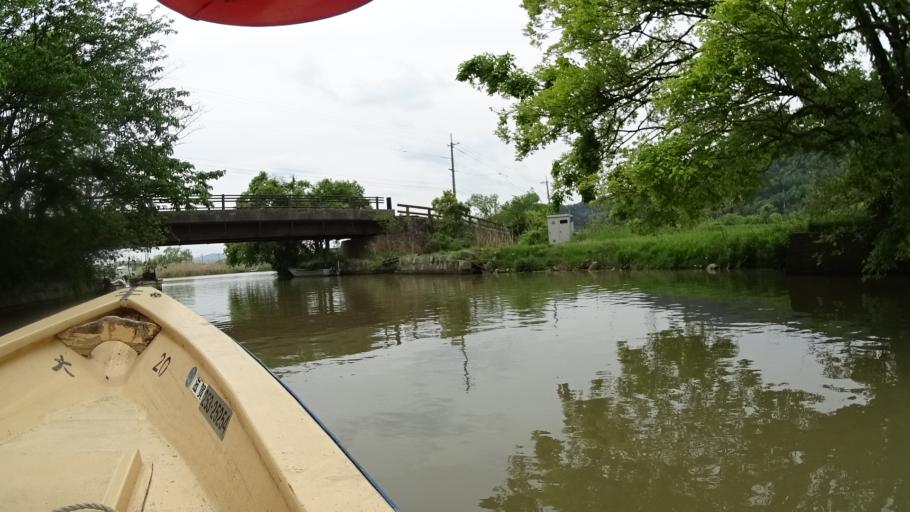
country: JP
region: Shiga Prefecture
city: Omihachiman
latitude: 35.1496
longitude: 136.0952
